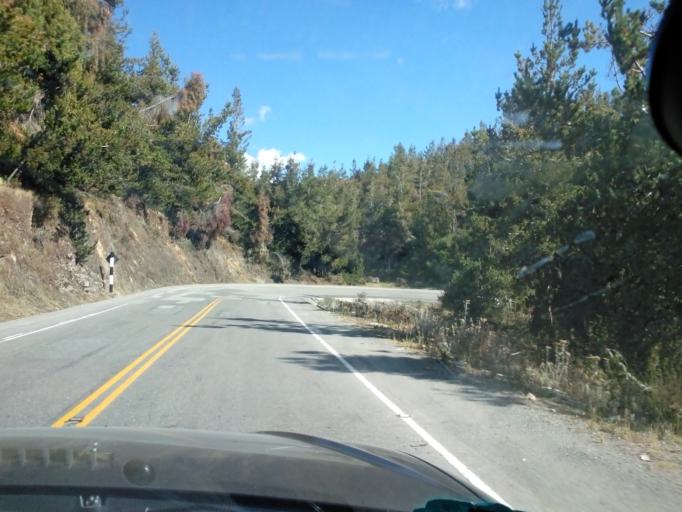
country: PE
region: Apurimac
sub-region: Provincia de Abancay
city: Cachora
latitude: -13.5646
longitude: -72.8219
